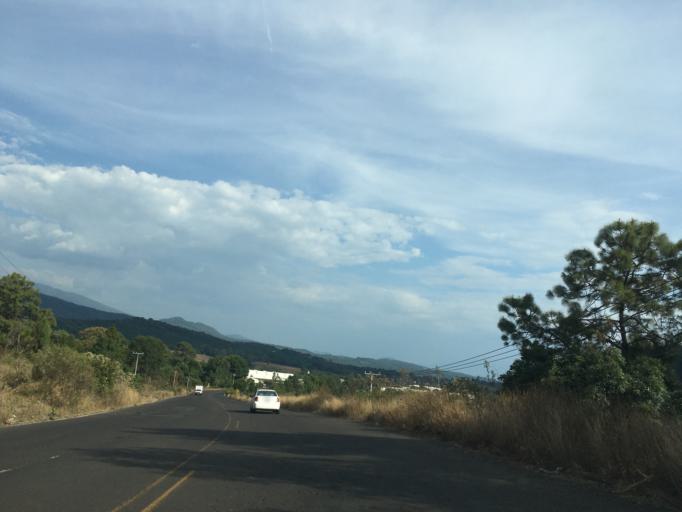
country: MX
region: Michoacan
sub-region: Tingueindin
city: Tingueindin
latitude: 19.7824
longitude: -102.5088
